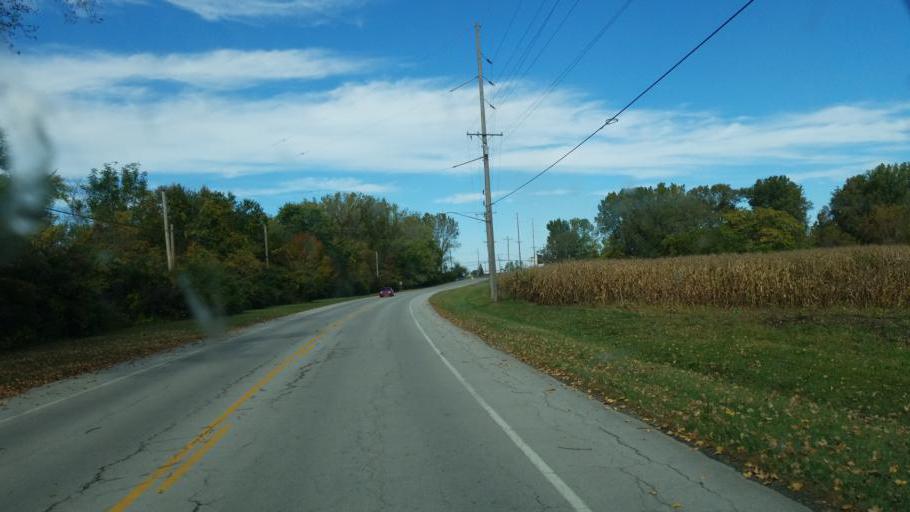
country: US
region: Ohio
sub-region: Erie County
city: Huron
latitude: 41.3860
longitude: -82.5500
